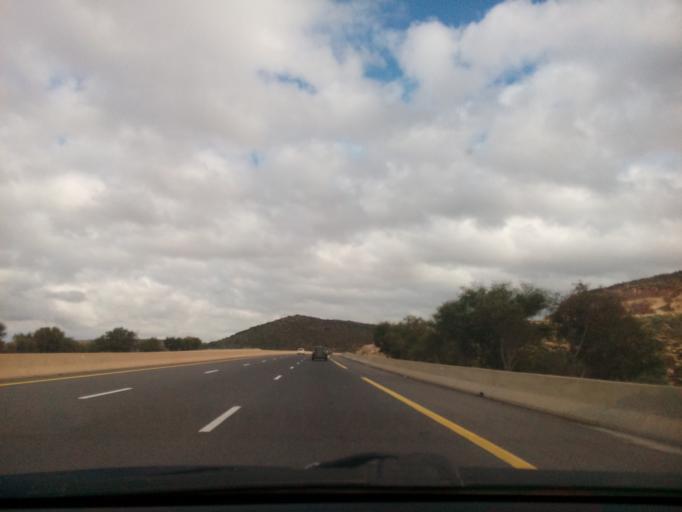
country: DZ
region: Tlemcen
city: Sidi Abdelli
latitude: 35.0177
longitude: -1.1482
